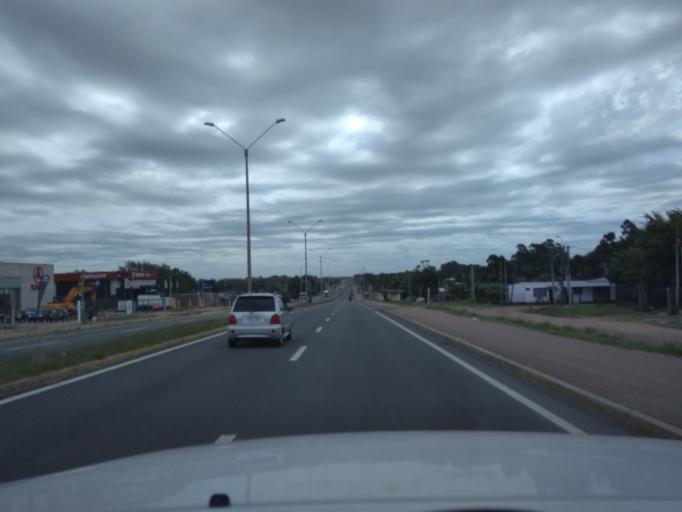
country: UY
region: Canelones
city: Colonia Nicolich
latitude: -34.8189
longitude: -56.0118
